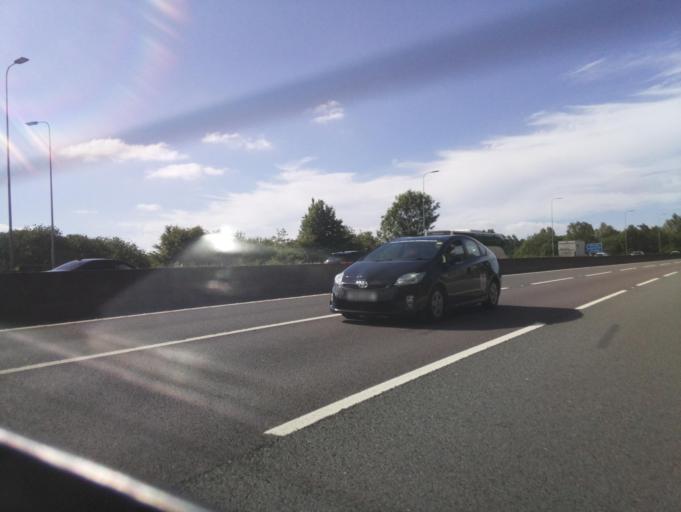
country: GB
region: England
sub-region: City and Borough of Salford
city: Walkden
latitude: 53.4968
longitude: -2.3847
